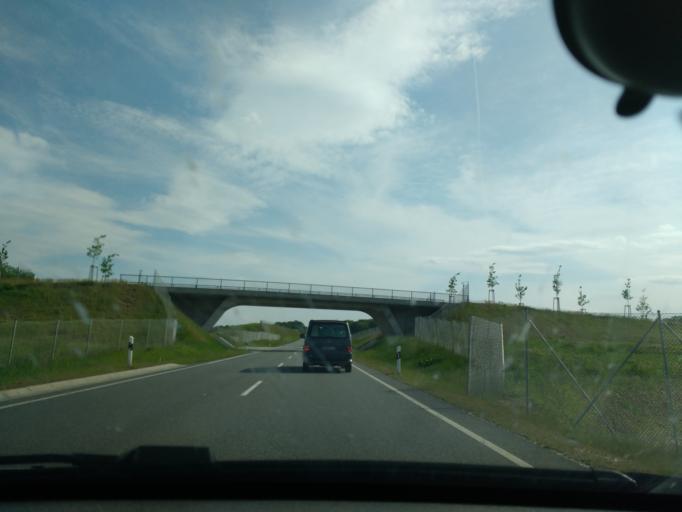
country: DE
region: Schleswig-Holstein
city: Pogeez
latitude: 53.7547
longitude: 10.7250
